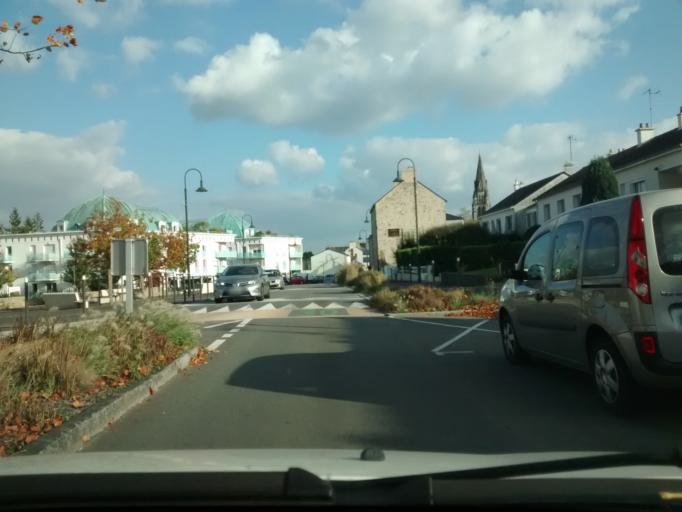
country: FR
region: Pays de la Loire
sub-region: Departement de la Loire-Atlantique
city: Orvault
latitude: 47.2721
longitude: -1.6261
